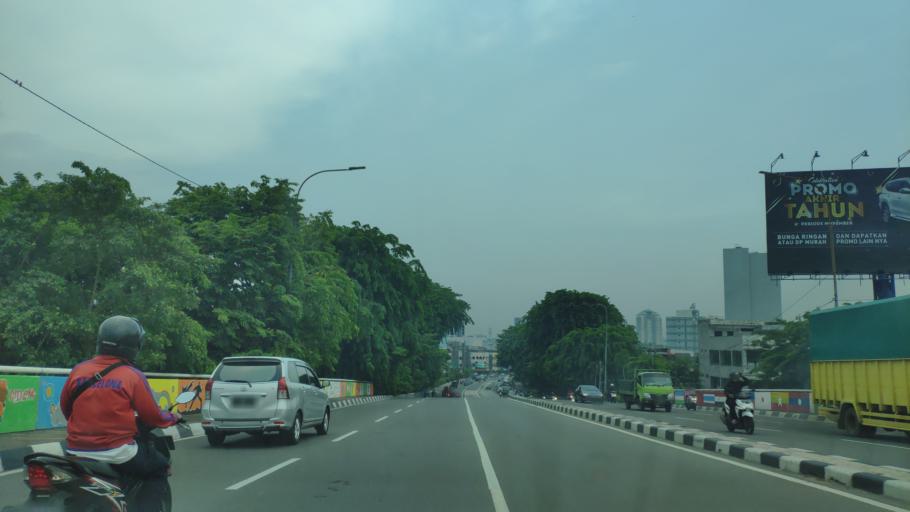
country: ID
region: Jakarta Raya
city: Jakarta
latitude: -6.1731
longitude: 106.8061
